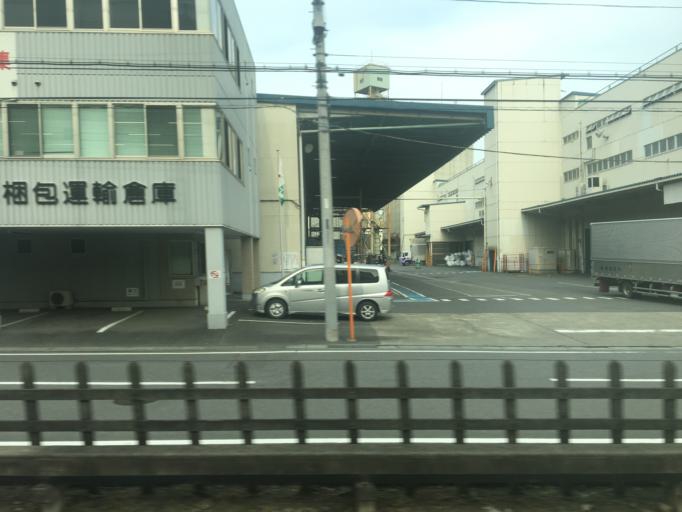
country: JP
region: Saitama
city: Sayama
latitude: 35.8776
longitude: 139.4382
